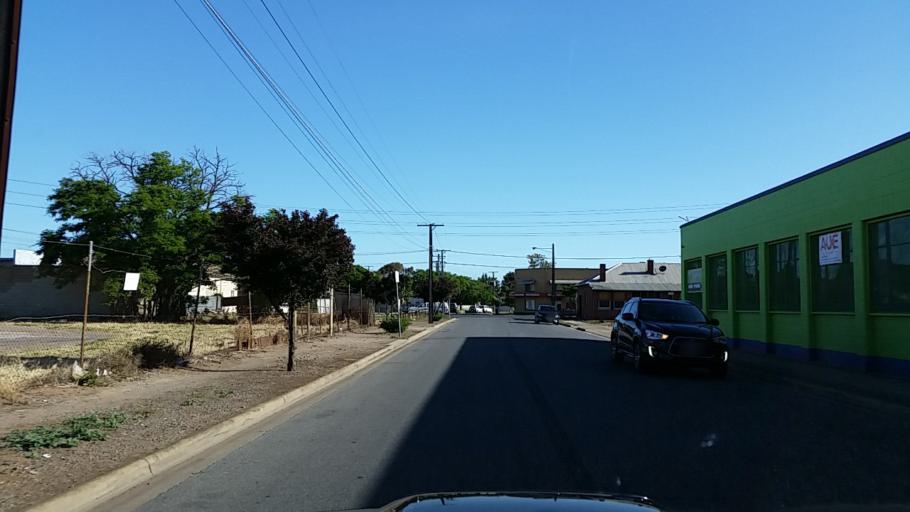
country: AU
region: South Australia
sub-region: Charles Sturt
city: Allenby Gardens
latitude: -34.9036
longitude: 138.5498
